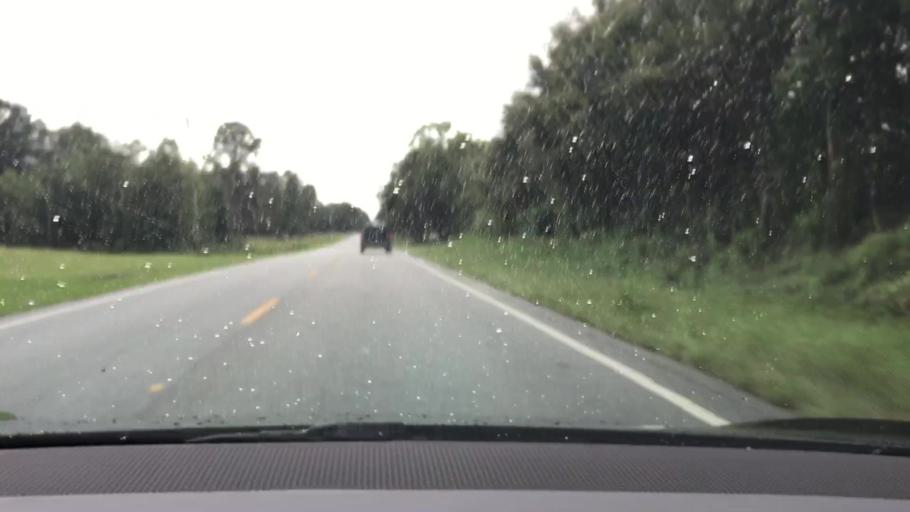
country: US
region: Alabama
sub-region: Geneva County
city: Samson
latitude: 31.1092
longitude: -86.1113
